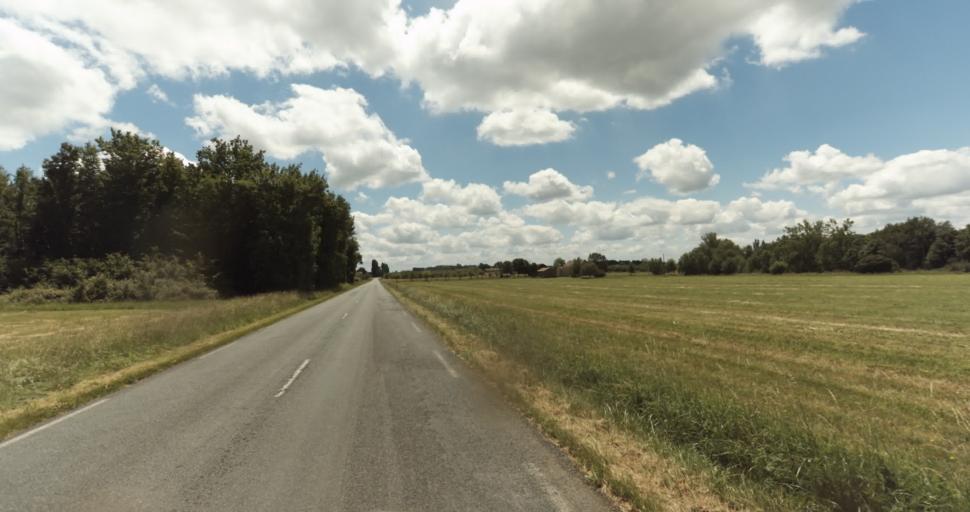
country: FR
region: Aquitaine
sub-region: Departement de la Dordogne
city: Beaumont-du-Perigord
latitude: 44.7451
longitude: 0.7802
